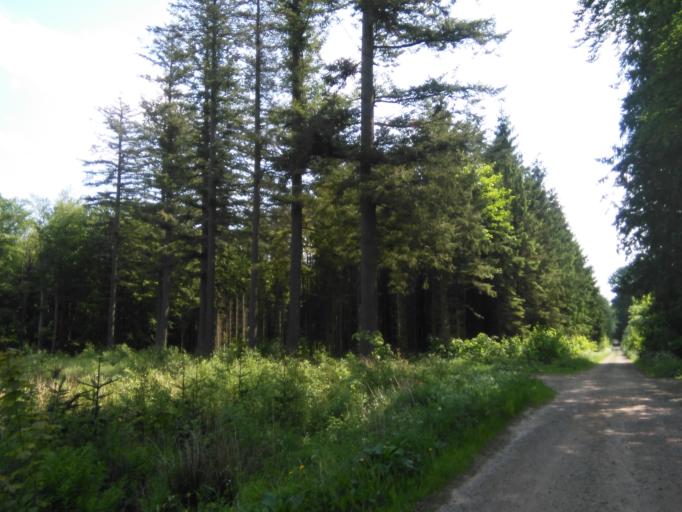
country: DK
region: Central Jutland
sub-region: Favrskov Kommune
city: Hinnerup
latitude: 56.2640
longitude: 10.0425
